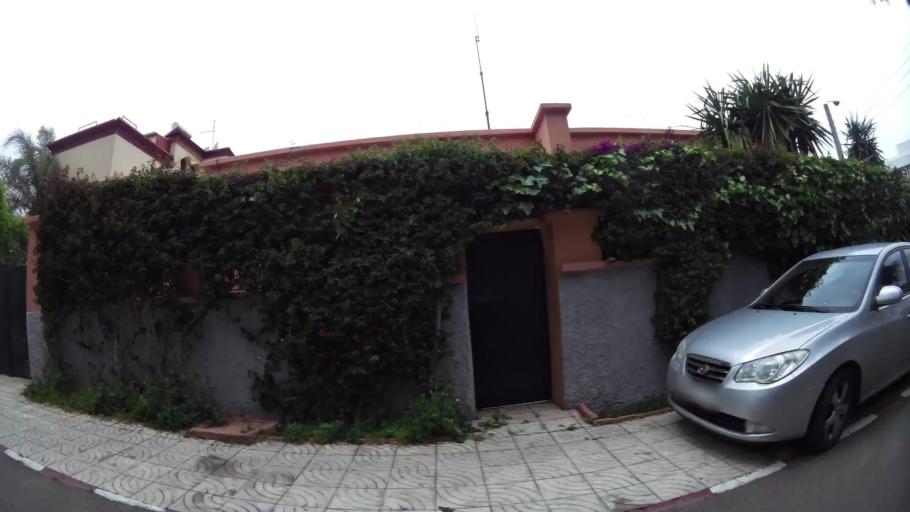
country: MA
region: Grand Casablanca
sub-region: Casablanca
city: Casablanca
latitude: 33.5628
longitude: -7.6310
